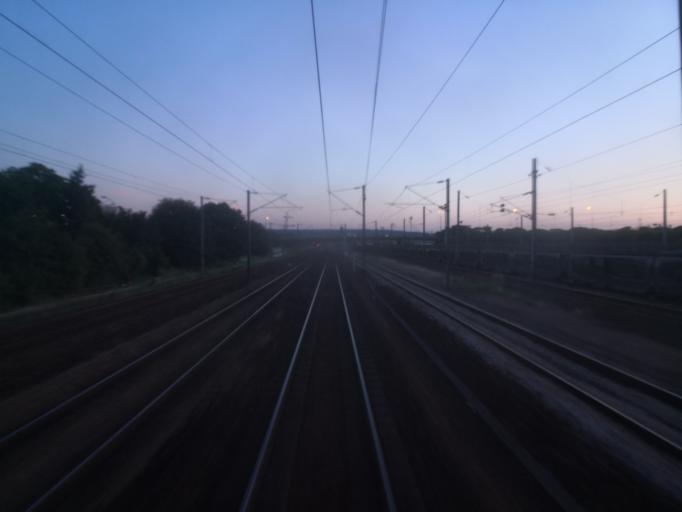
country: FR
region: Ile-de-France
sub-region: Departement des Yvelines
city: Poissy
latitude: 48.9405
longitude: 2.0574
